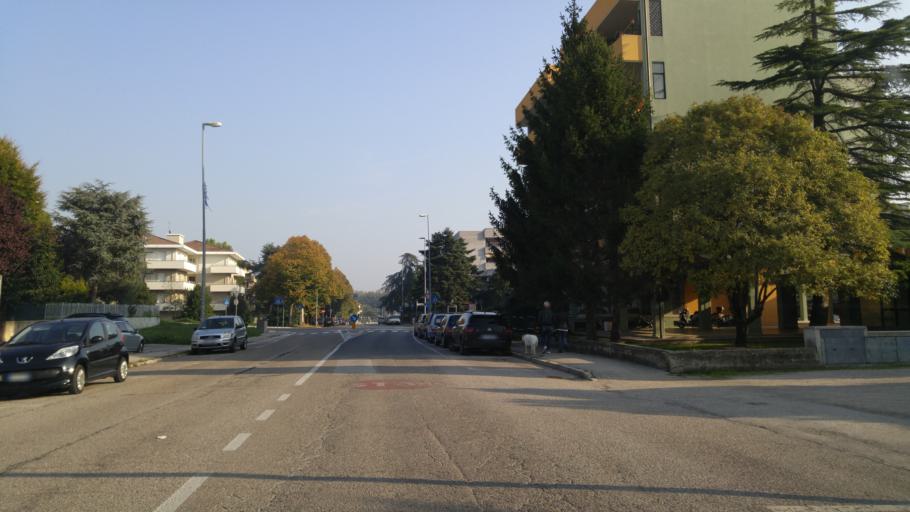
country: IT
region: The Marches
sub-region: Provincia di Pesaro e Urbino
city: Pesaro
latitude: 43.9128
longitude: 12.8673
